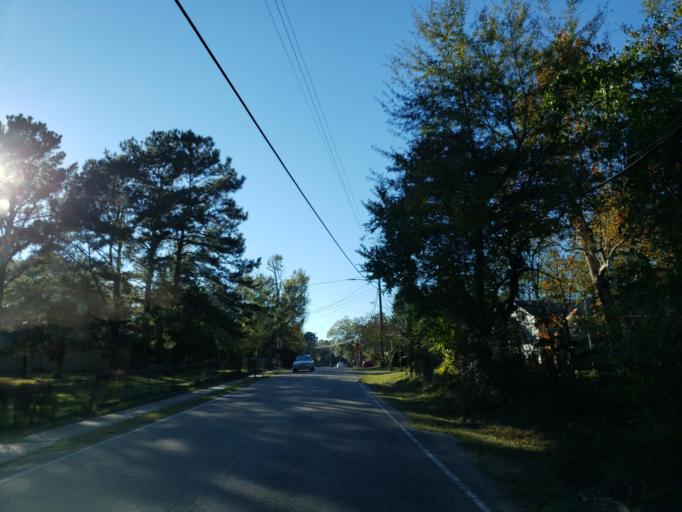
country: US
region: Mississippi
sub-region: Forrest County
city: Hattiesburg
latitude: 31.2775
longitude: -89.2700
